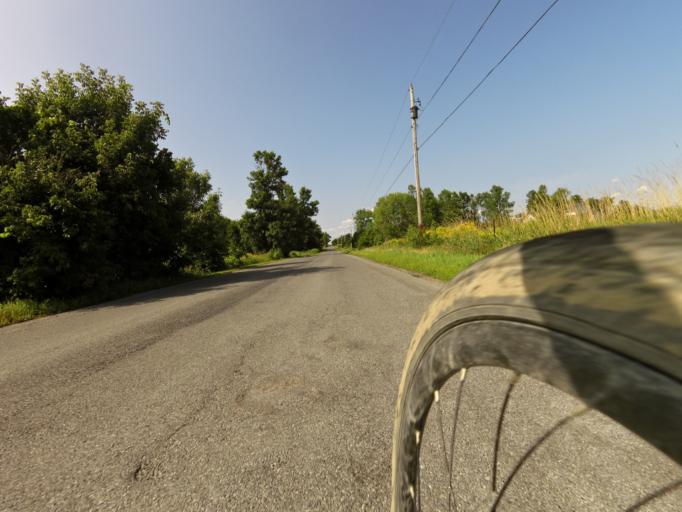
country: CA
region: Ontario
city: Kingston
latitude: 44.3126
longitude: -76.6715
